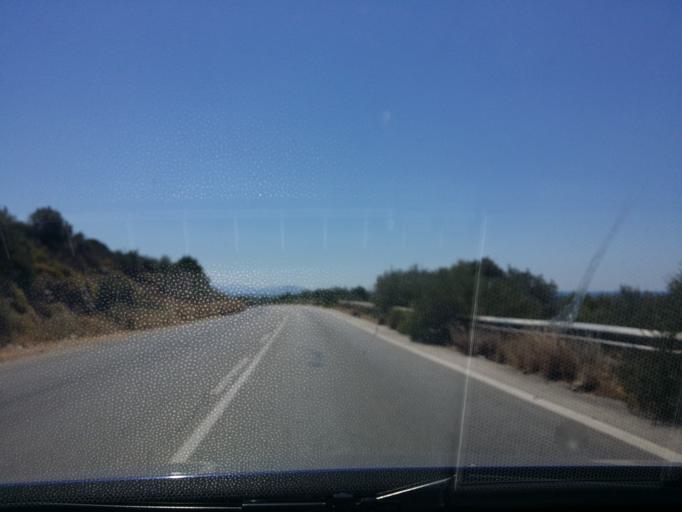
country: GR
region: Peloponnese
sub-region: Nomos Lakonias
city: Skala
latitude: 36.8519
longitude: 22.6123
